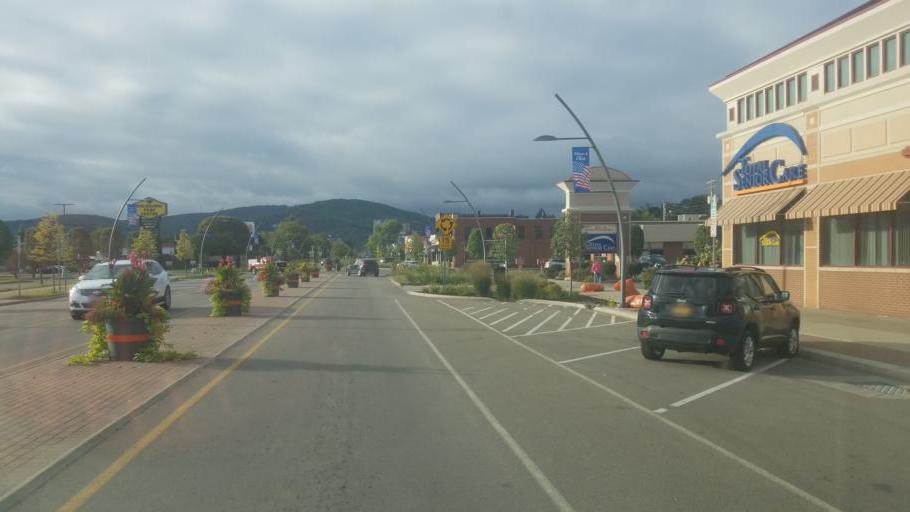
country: US
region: New York
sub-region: Cattaraugus County
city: Olean
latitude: 42.0861
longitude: -78.4300
